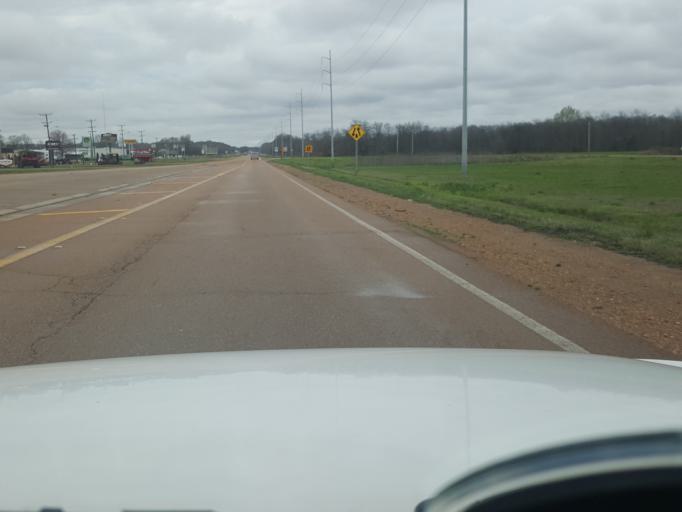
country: US
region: Mississippi
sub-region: Yazoo County
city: Yazoo City
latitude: 32.8582
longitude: -90.4293
